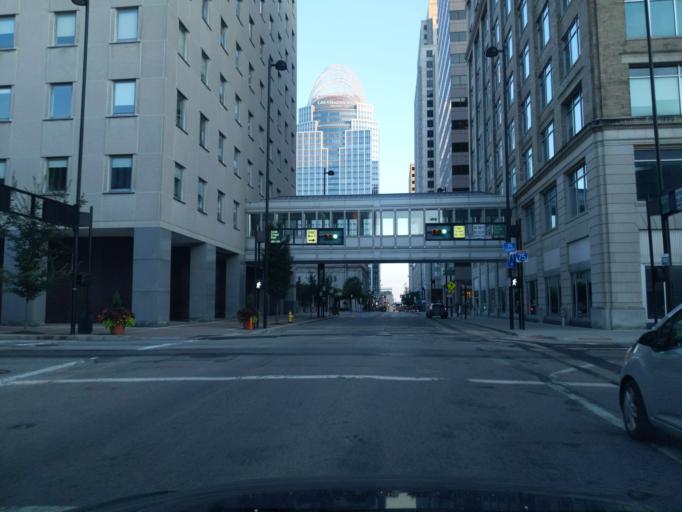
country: US
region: Kentucky
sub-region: Campbell County
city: Newport
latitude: 39.1033
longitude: -84.5085
